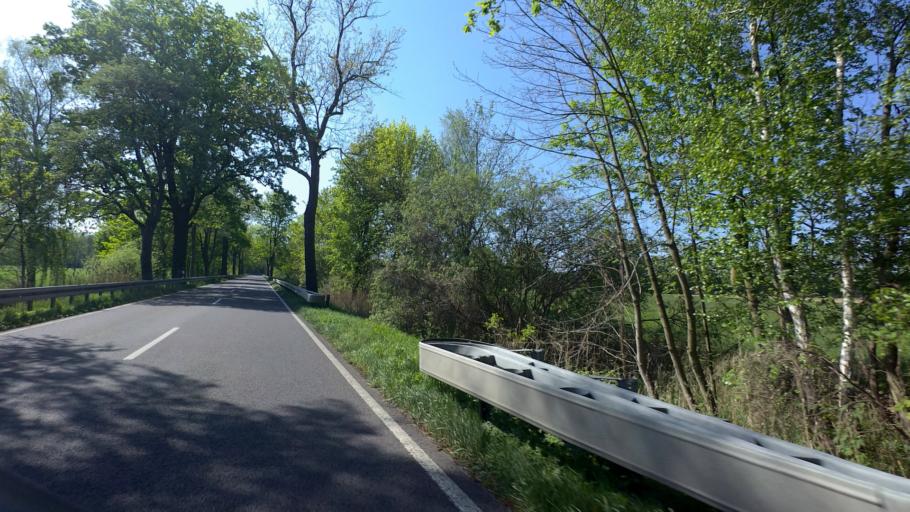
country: DE
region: Brandenburg
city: Schlepzig
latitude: 52.0622
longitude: 13.9290
